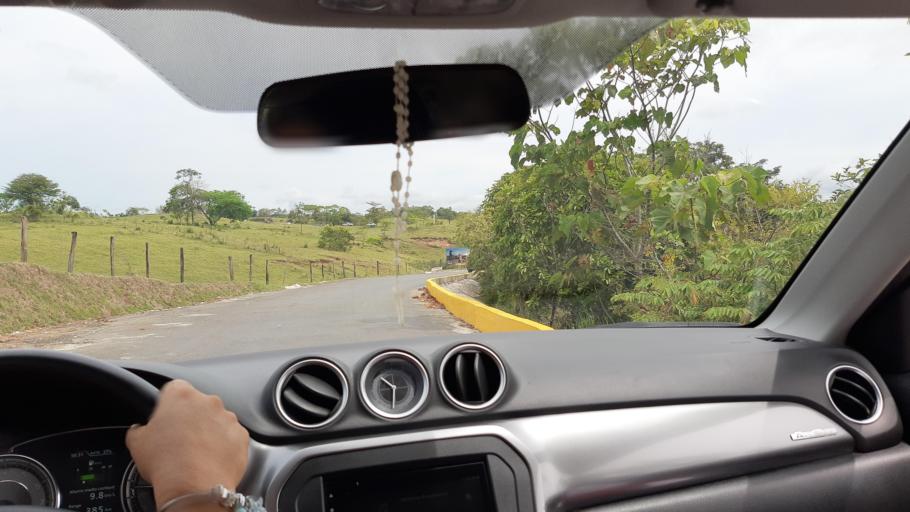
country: CO
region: Antioquia
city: Puerto Triunfo
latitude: 5.9036
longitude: -74.7207
